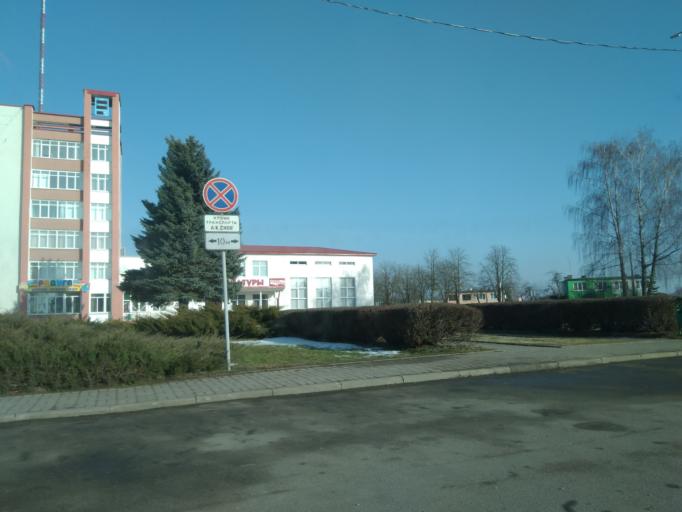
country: BY
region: Minsk
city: Snow
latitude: 53.2218
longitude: 26.4000
